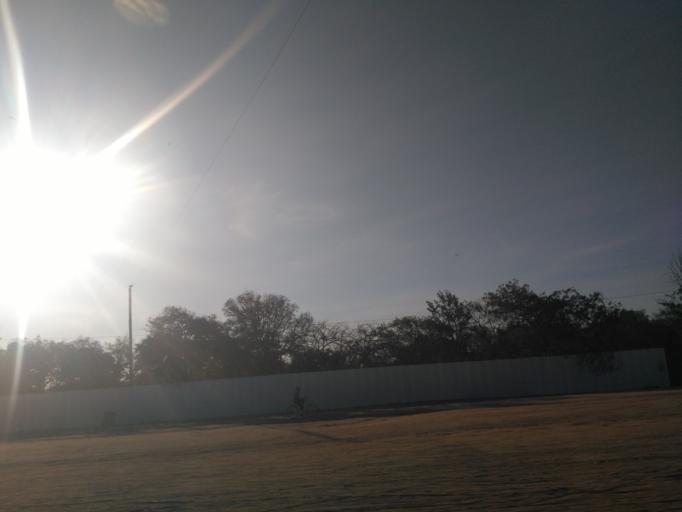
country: TZ
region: Dodoma
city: Dodoma
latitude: -6.1686
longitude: 35.7434
